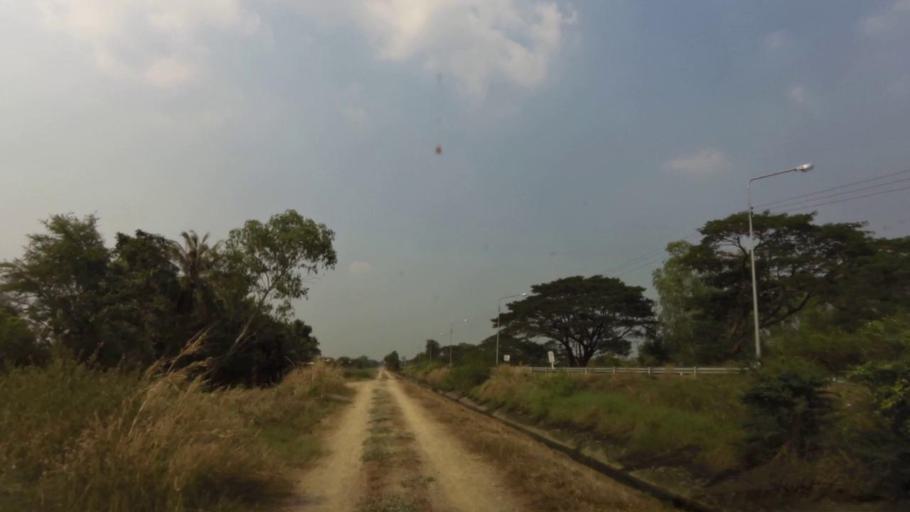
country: TH
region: Phra Nakhon Si Ayutthaya
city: Phra Nakhon Si Ayutthaya
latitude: 14.3126
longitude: 100.5619
